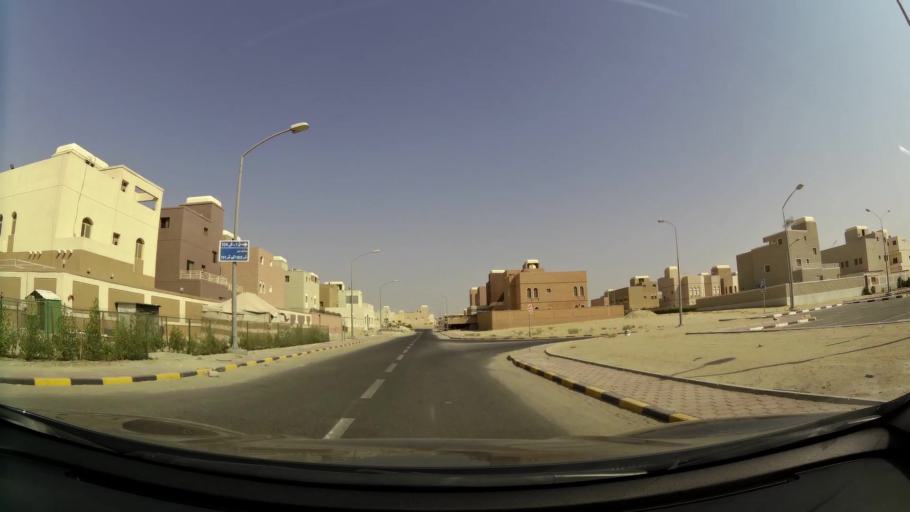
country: KW
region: Al Ahmadi
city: Al Wafrah
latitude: 28.8062
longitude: 48.0489
